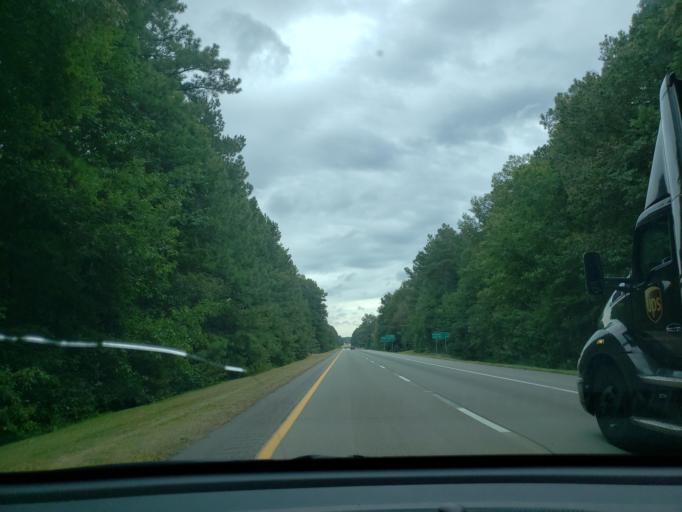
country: US
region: North Carolina
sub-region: Granville County
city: Oxford
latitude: 36.3211
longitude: -78.5098
